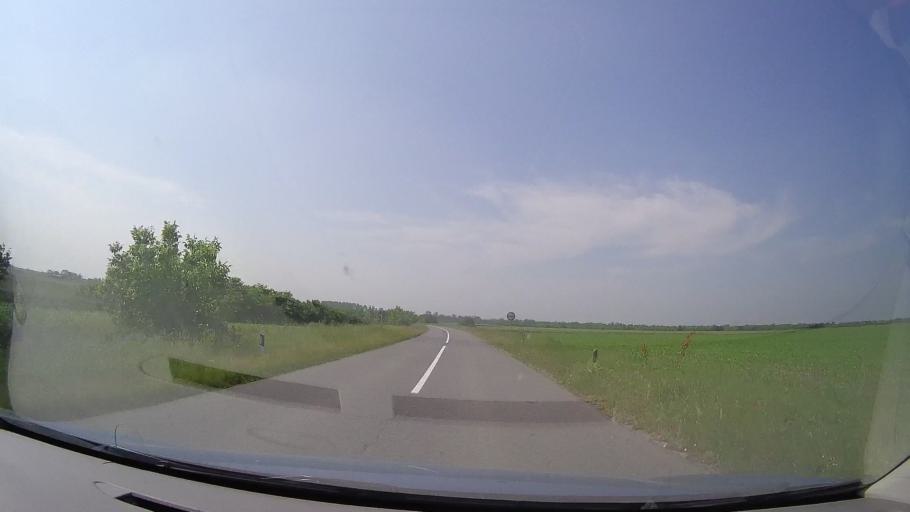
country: RS
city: Jarkovac
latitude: 45.2825
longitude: 20.7628
